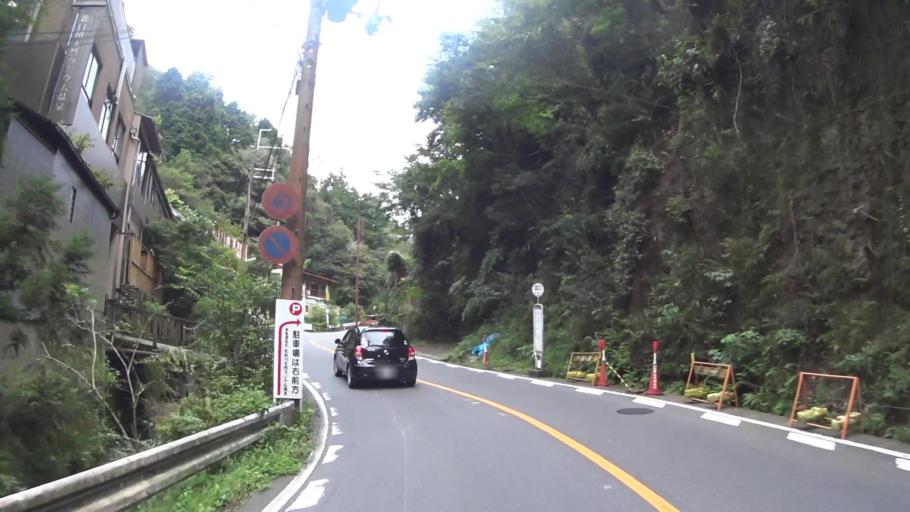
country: JP
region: Kyoto
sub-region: Kyoto-shi
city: Kamigyo-ku
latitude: 35.0376
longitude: 135.8096
